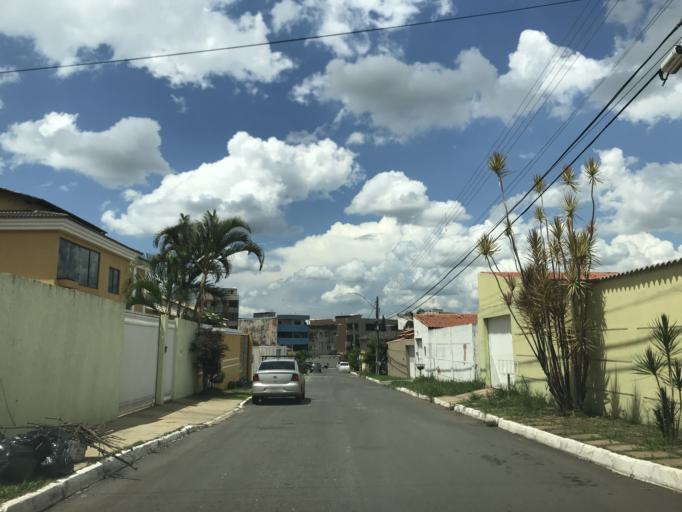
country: BR
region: Federal District
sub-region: Brasilia
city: Brasilia
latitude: -15.6830
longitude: -47.8350
